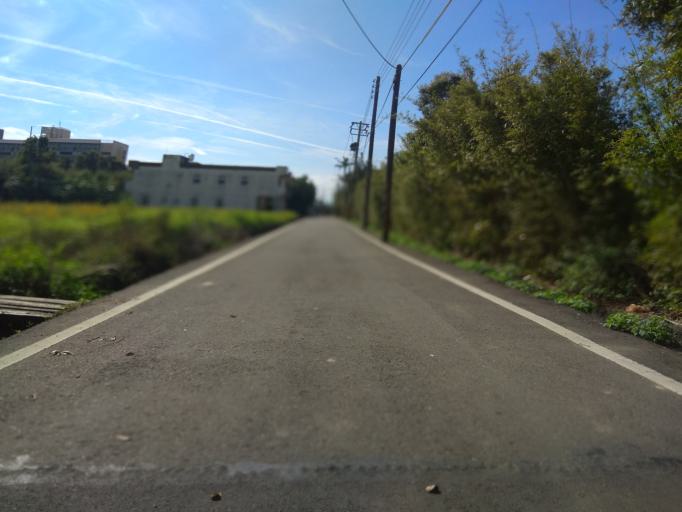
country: TW
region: Taiwan
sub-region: Hsinchu
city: Zhubei
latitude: 24.9898
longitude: 121.0406
